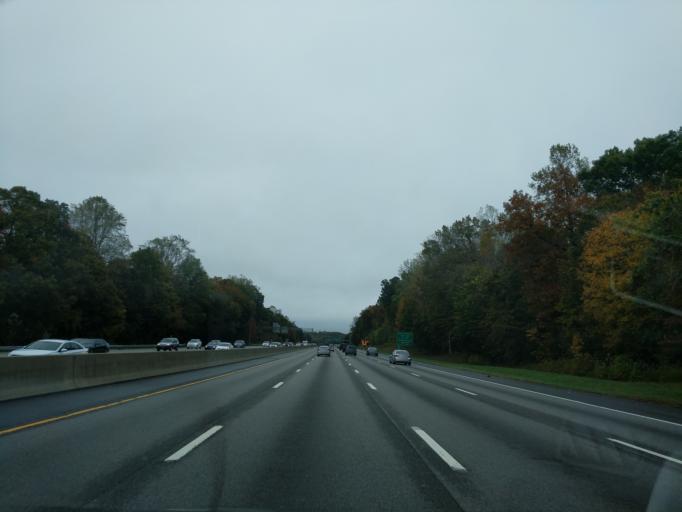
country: US
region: North Carolina
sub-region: Orange County
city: Hillsborough
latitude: 36.0659
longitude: -79.1442
